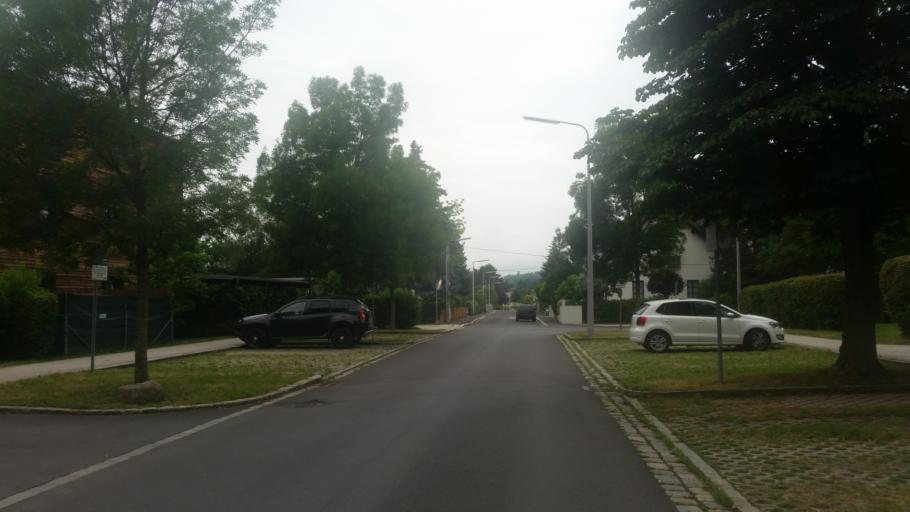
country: AT
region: Upper Austria
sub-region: Politischer Bezirk Linz-Land
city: Leonding
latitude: 48.2685
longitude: 14.2777
